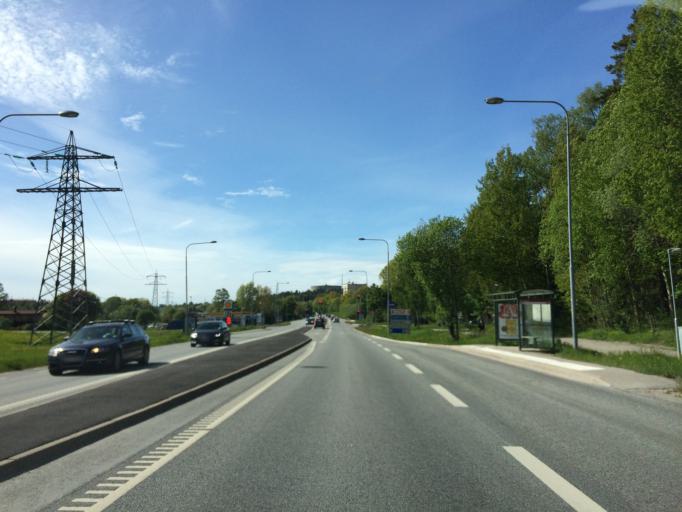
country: SE
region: Stockholm
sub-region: Sollentuna Kommun
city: Sollentuna
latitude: 59.4429
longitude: 17.9679
